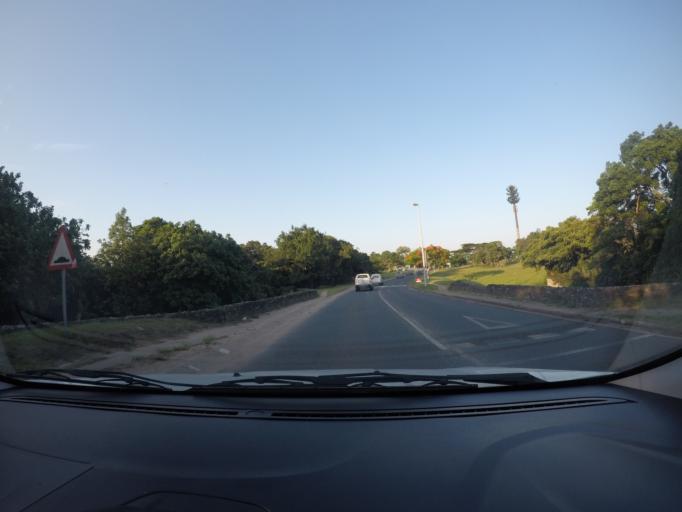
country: ZA
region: KwaZulu-Natal
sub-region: uThungulu District Municipality
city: Richards Bay
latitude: -28.7791
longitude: 32.0998
